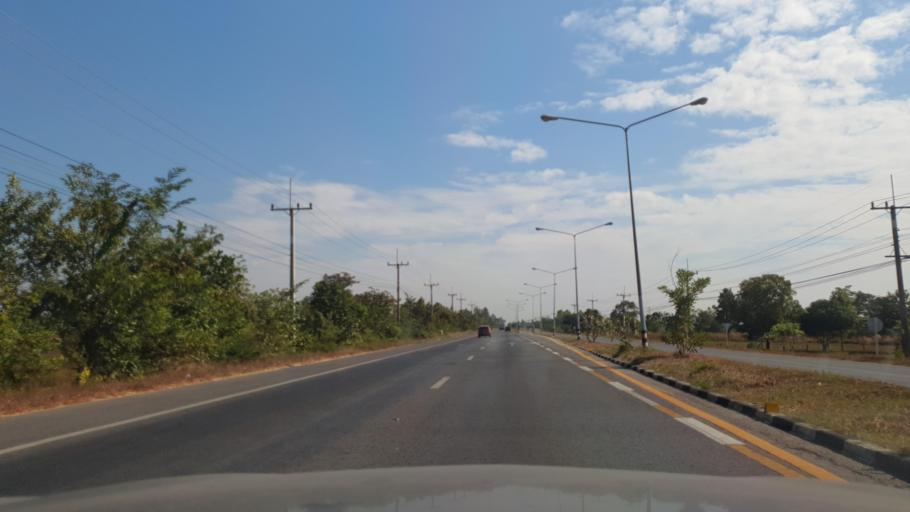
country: TH
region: Maha Sarakham
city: Kantharawichai
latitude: 16.3840
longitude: 103.2258
